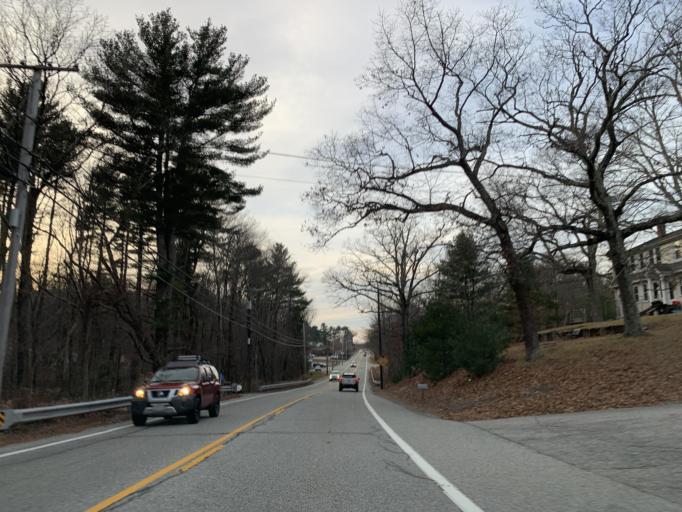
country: US
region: Rhode Island
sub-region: Providence County
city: Chepachet
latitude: 41.9057
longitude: -71.6570
